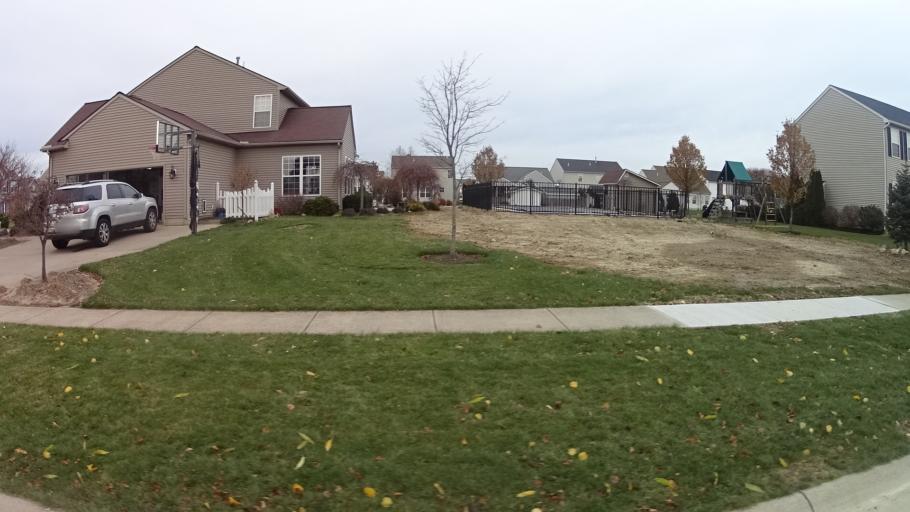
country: US
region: Ohio
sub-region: Lorain County
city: Avon
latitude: 41.4140
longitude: -82.0533
